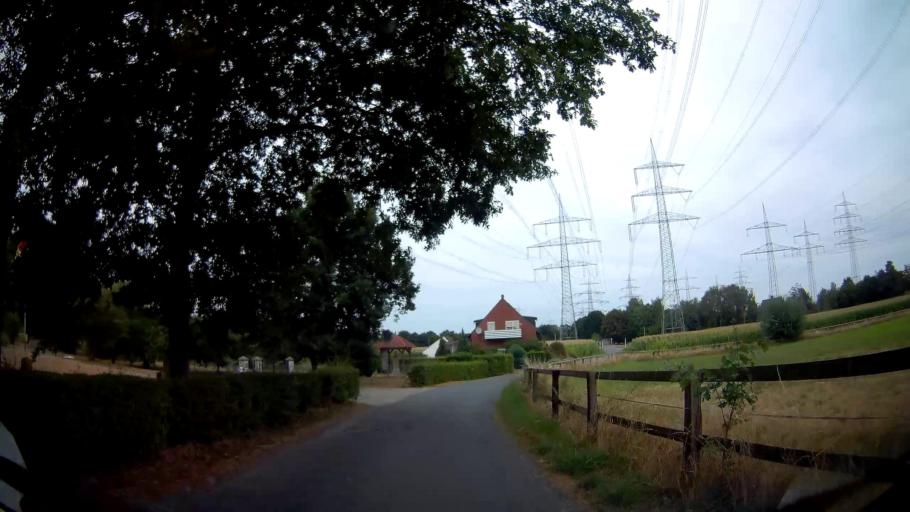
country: DE
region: North Rhine-Westphalia
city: Marl
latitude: 51.6794
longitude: 7.0614
